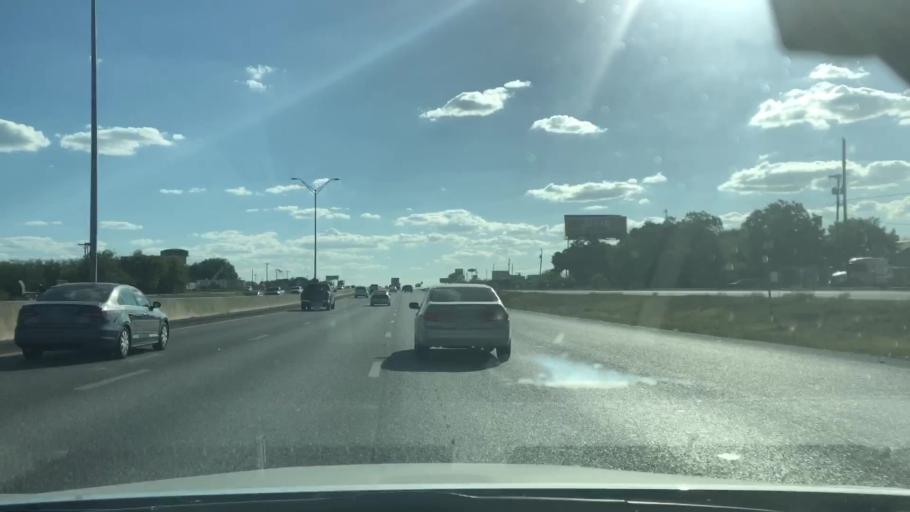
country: US
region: Texas
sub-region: Comal County
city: New Braunfels
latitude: 29.6622
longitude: -98.1730
